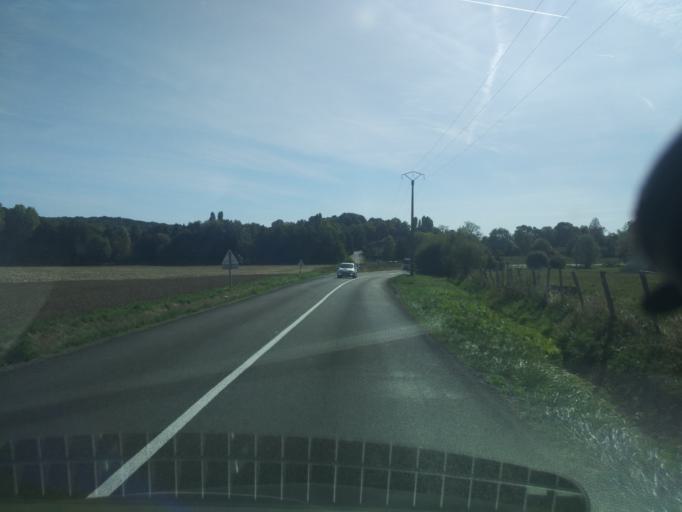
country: FR
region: Ile-de-France
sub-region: Departement de l'Essonne
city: Briis-sous-Forges
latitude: 48.6299
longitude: 2.1160
